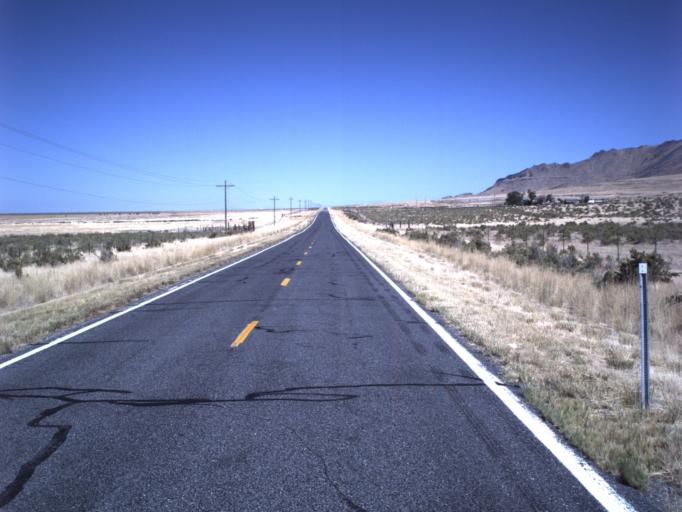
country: US
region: Utah
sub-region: Tooele County
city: Grantsville
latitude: 40.6785
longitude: -112.6718
